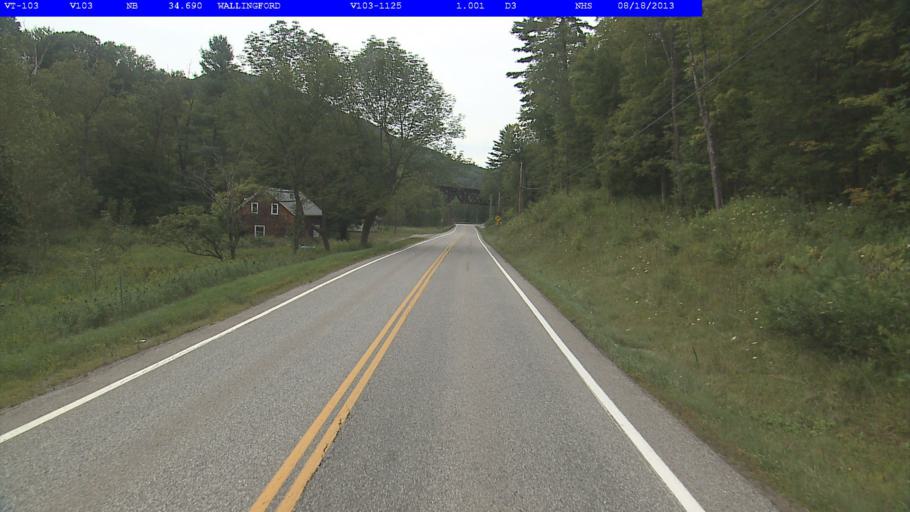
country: US
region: Vermont
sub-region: Rutland County
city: Rutland
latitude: 43.4608
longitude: -72.8800
